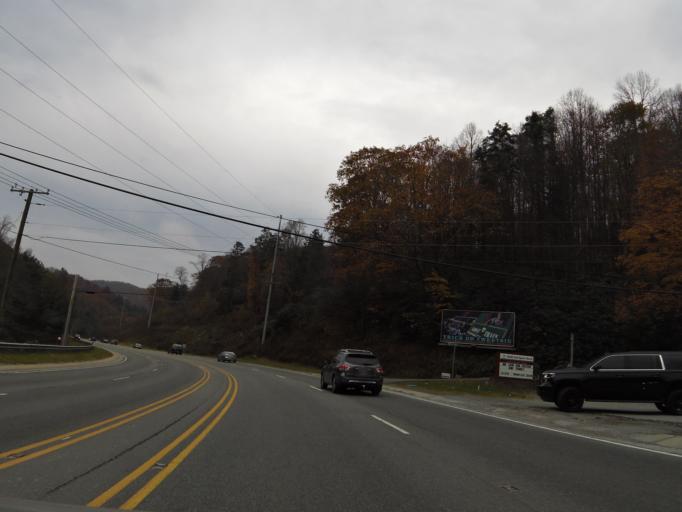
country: US
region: North Carolina
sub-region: Watauga County
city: Blowing Rock
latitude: 36.1745
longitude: -81.6486
